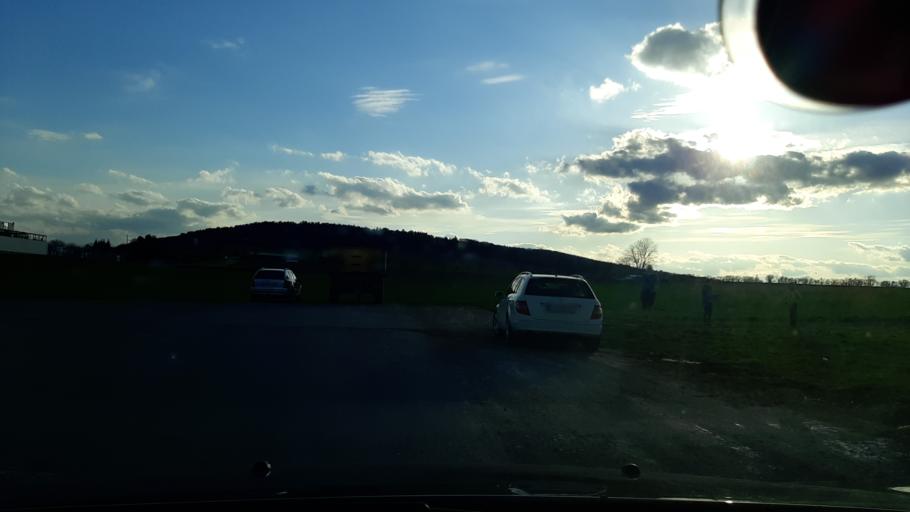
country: DE
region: North Rhine-Westphalia
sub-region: Regierungsbezirk Koln
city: Mechernich
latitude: 50.6202
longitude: 6.6492
